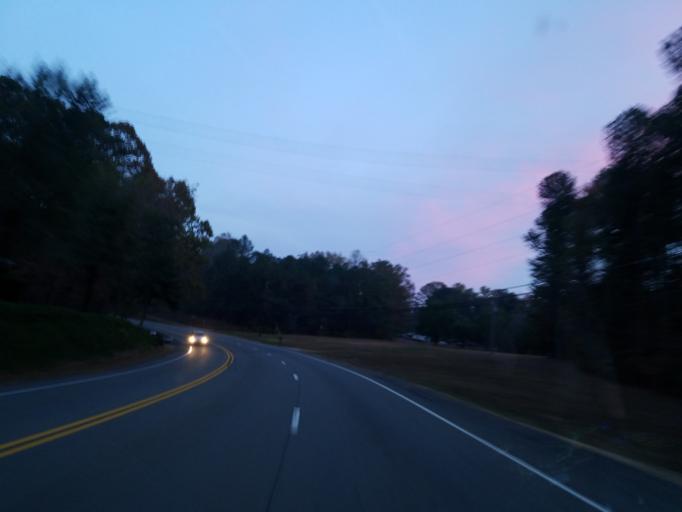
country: US
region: Georgia
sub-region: Pickens County
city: Jasper
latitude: 34.4939
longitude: -84.4685
